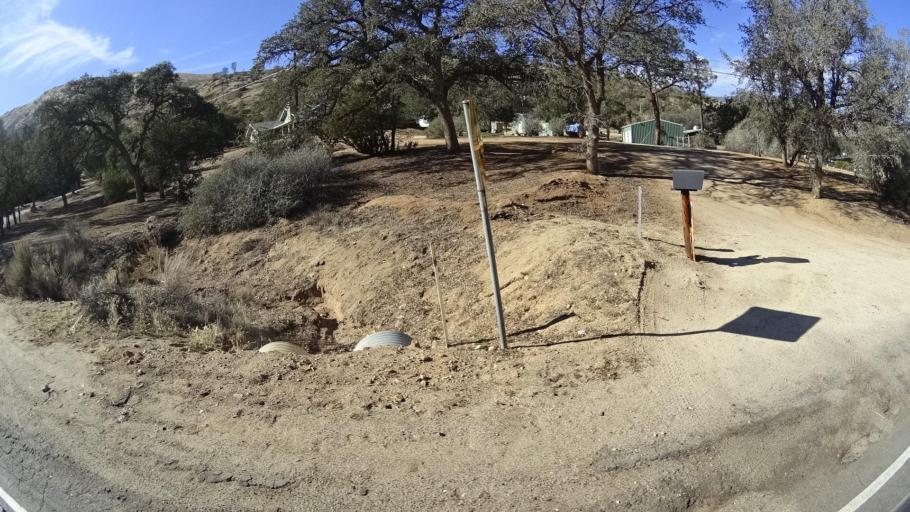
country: US
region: California
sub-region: Kern County
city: Bodfish
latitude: 35.5854
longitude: -118.4977
